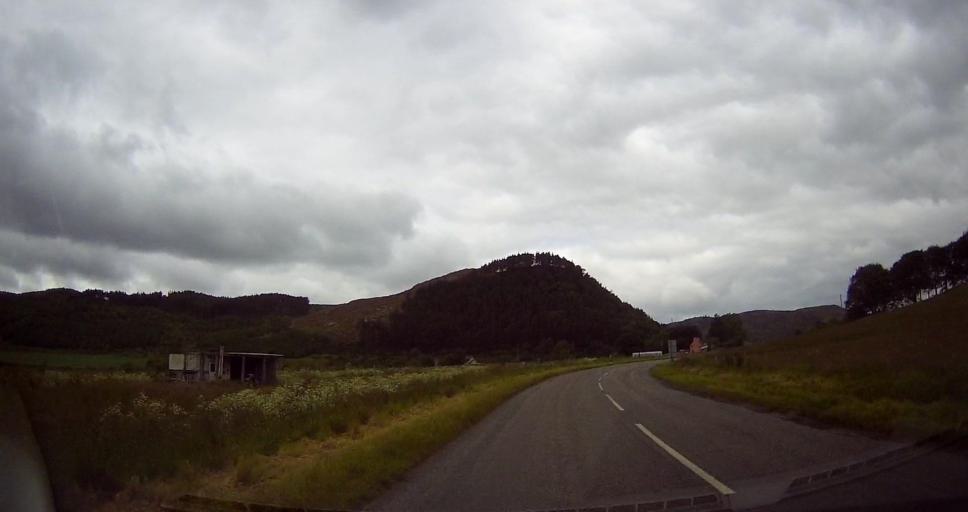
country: GB
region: Scotland
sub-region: Highland
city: Dornoch
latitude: 57.9929
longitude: -4.1697
